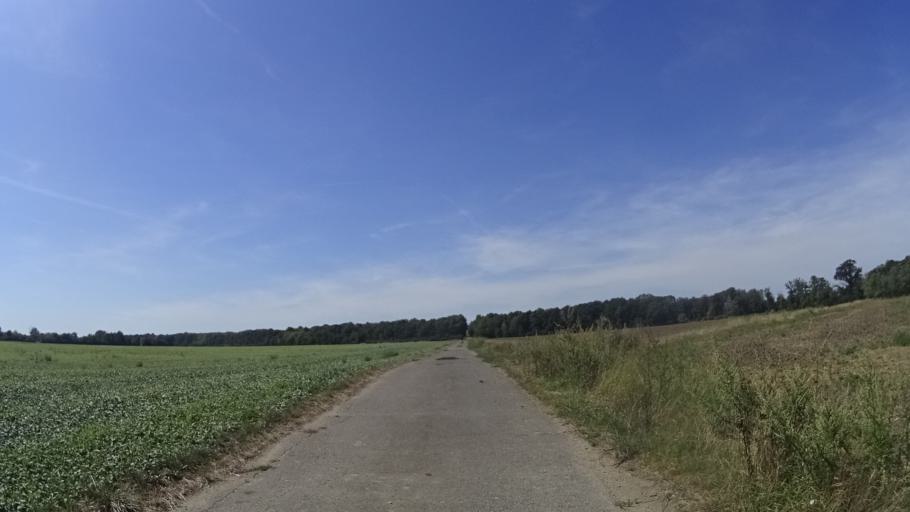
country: AT
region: Lower Austria
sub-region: Politischer Bezirk Ganserndorf
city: Angern an der March
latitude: 48.3674
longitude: 16.8639
